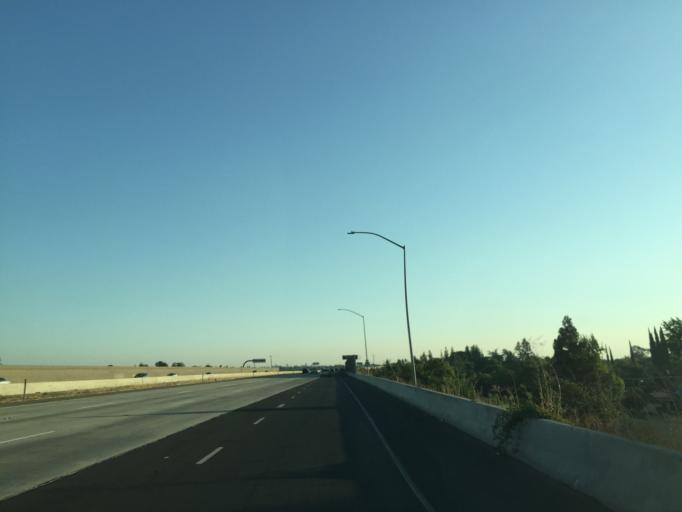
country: US
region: California
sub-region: Fresno County
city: Tarpey Village
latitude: 36.8052
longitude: -119.7369
